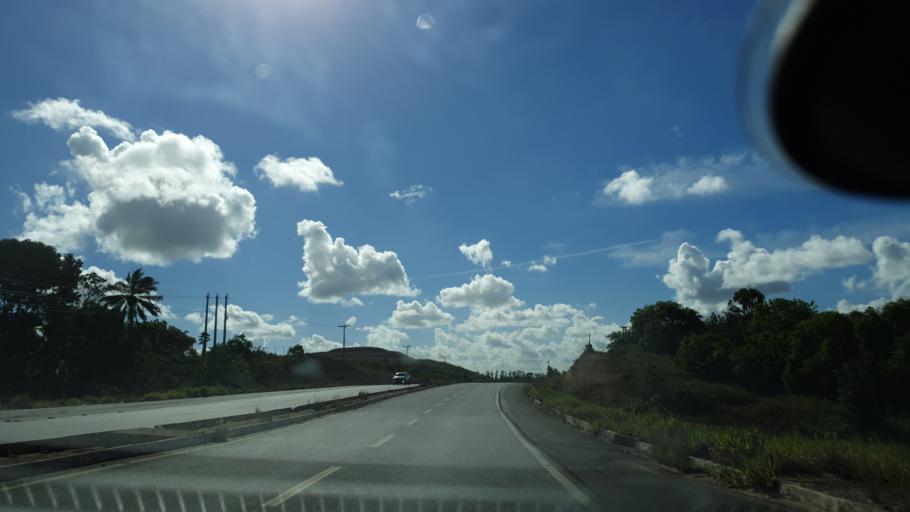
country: BR
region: Bahia
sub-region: Camacari
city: Camacari
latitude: -12.6852
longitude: -38.2531
